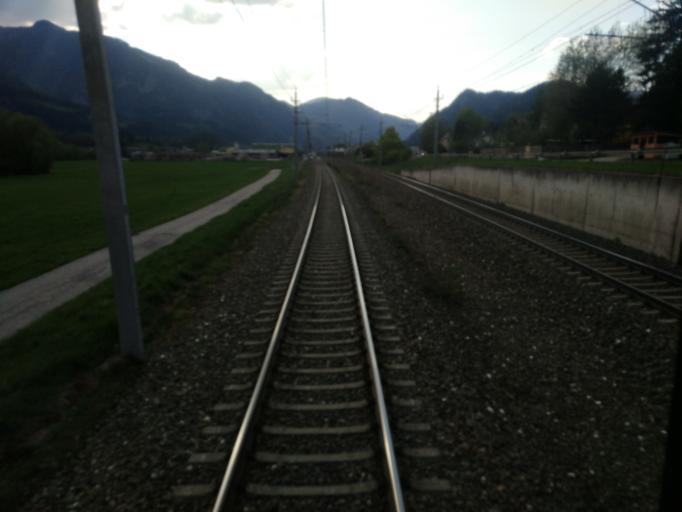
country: AT
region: Styria
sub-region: Politischer Bezirk Leoben
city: Mautern in Steiermark
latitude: 47.3965
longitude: 14.8424
